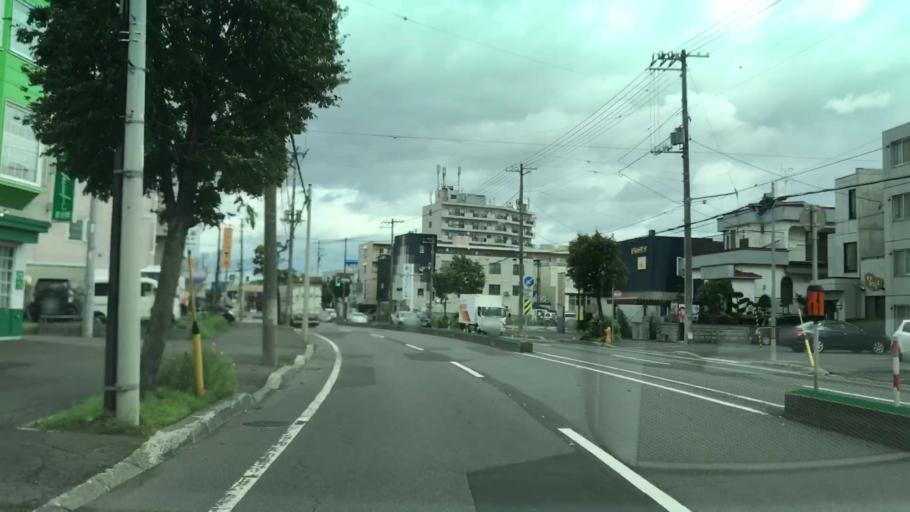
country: JP
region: Hokkaido
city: Sapporo
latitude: 42.9949
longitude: 141.4416
